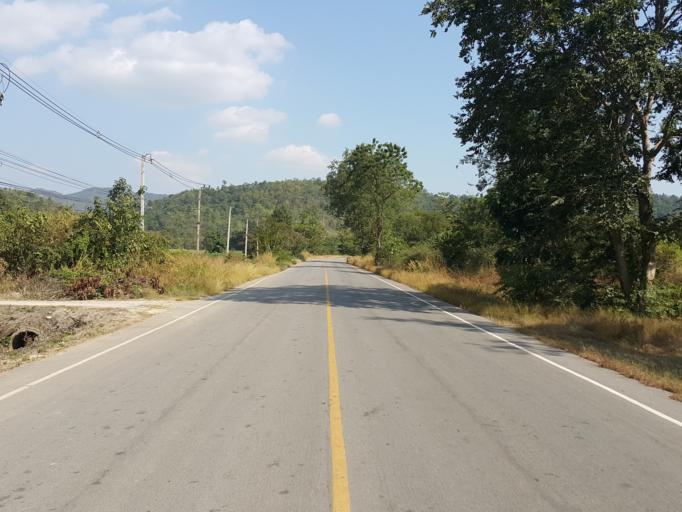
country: TH
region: Sukhothai
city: Thung Saliam
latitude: 17.3427
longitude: 99.4665
